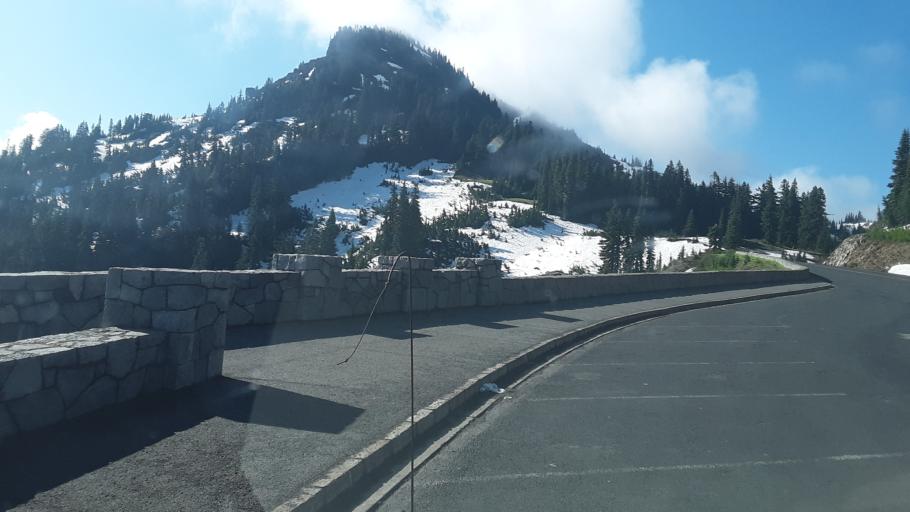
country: US
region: Washington
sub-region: King County
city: Enumclaw
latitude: 46.8743
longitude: -121.5160
